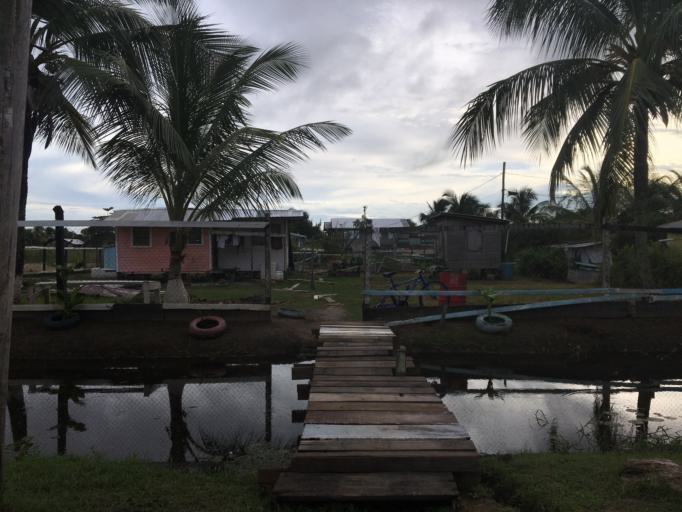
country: GY
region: Demerara-Mahaica
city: Georgetown
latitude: 6.7953
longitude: -58.1182
